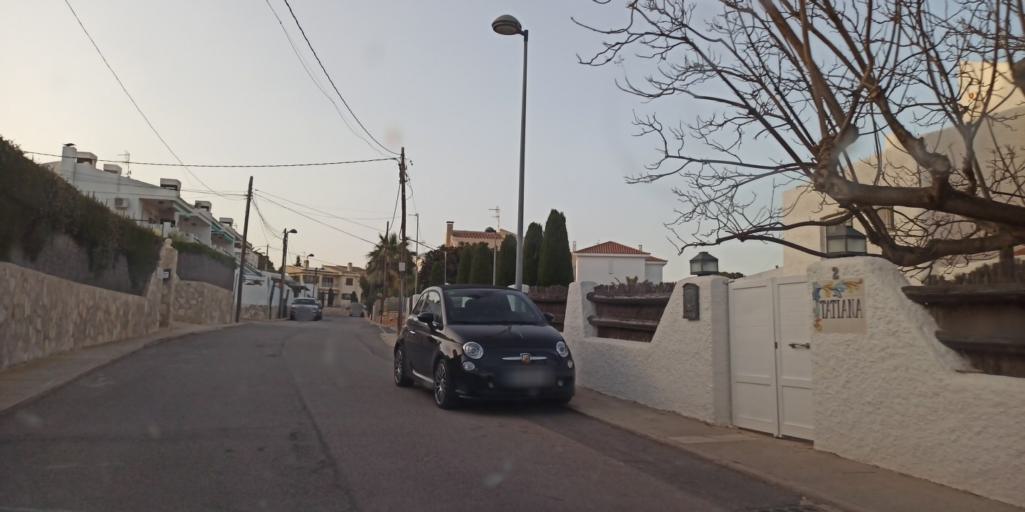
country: ES
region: Catalonia
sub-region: Provincia de Tarragona
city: L'Ampolla
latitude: 40.8152
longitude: 0.7209
